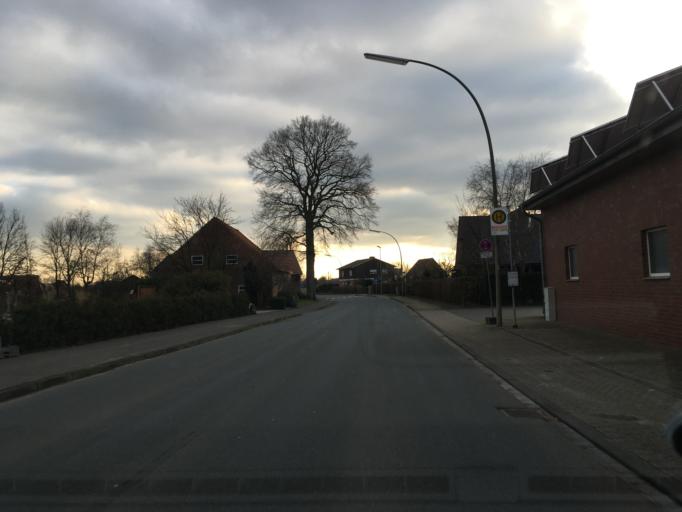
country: DE
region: North Rhine-Westphalia
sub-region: Regierungsbezirk Munster
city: Ahaus
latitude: 52.1314
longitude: 6.9886
